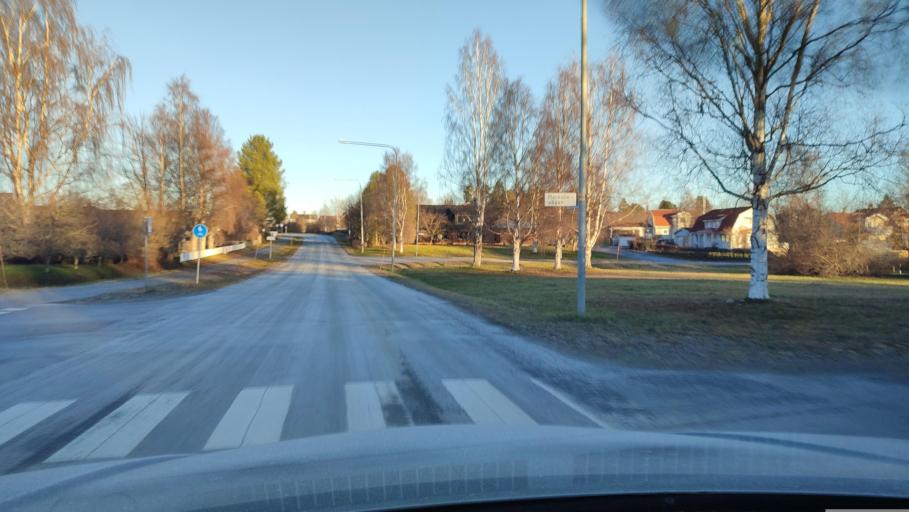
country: SE
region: Vaesterbotten
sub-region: Skelleftea Kommun
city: Viken
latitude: 64.7422
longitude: 20.9194
